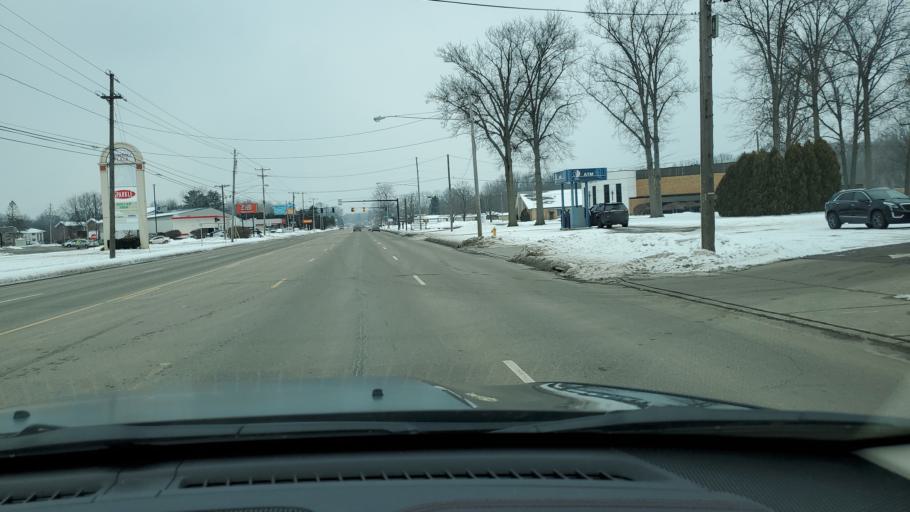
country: US
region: Ohio
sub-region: Trumbull County
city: Leavittsburg
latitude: 41.2519
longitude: -80.8552
